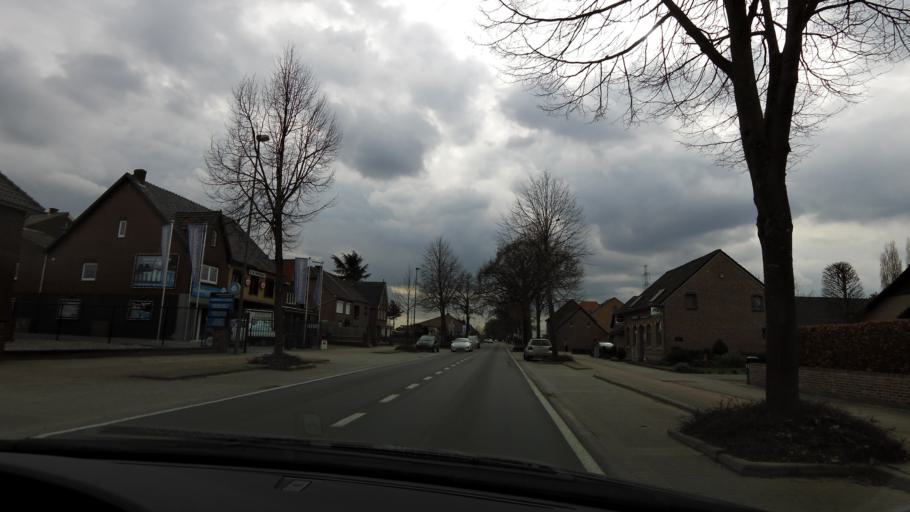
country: BE
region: Flanders
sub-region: Provincie Limburg
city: Maaseik
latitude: 51.1239
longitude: 5.8016
